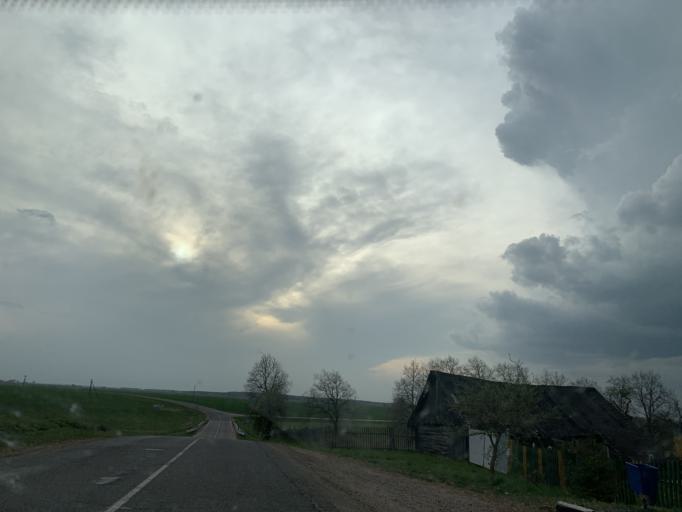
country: BY
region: Minsk
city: Kapyl'
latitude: 53.2907
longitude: 27.0054
